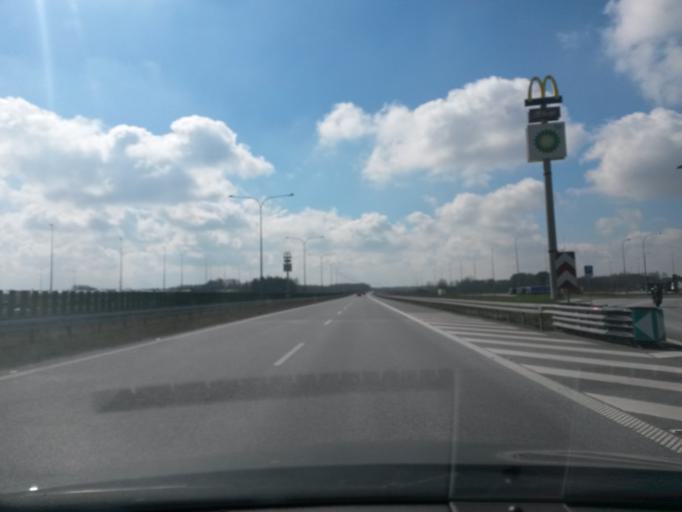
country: PL
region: Lodz Voivodeship
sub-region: powiat Lowicki
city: Bobrowniki
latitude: 52.0295
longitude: 20.0058
